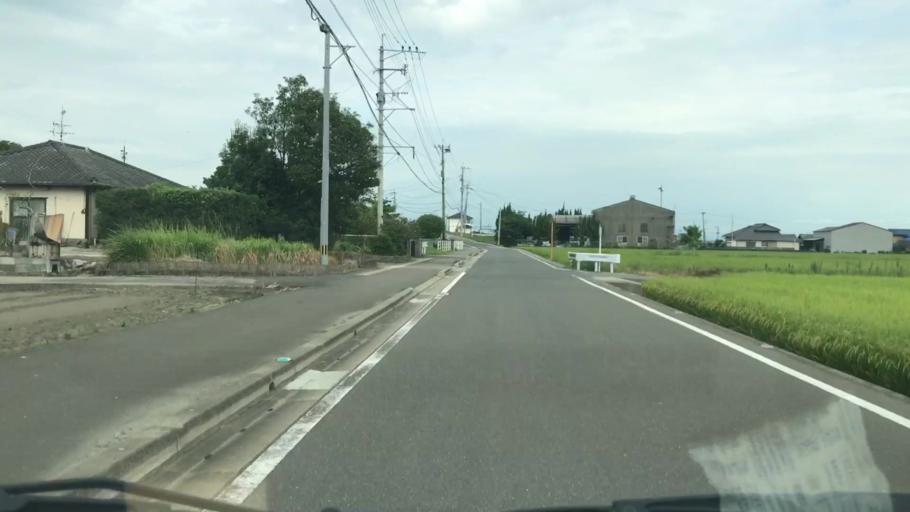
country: JP
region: Saga Prefecture
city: Saga-shi
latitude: 33.2895
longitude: 130.2264
